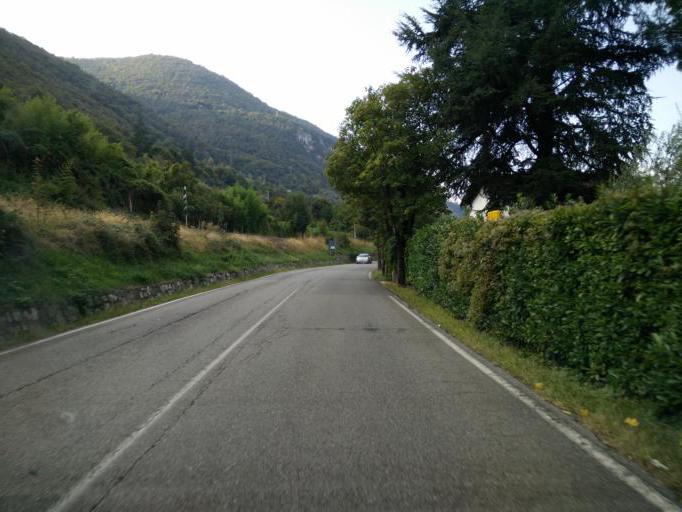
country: IT
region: Lombardy
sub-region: Provincia di Brescia
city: Sulzano
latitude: 45.6817
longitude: 10.0919
